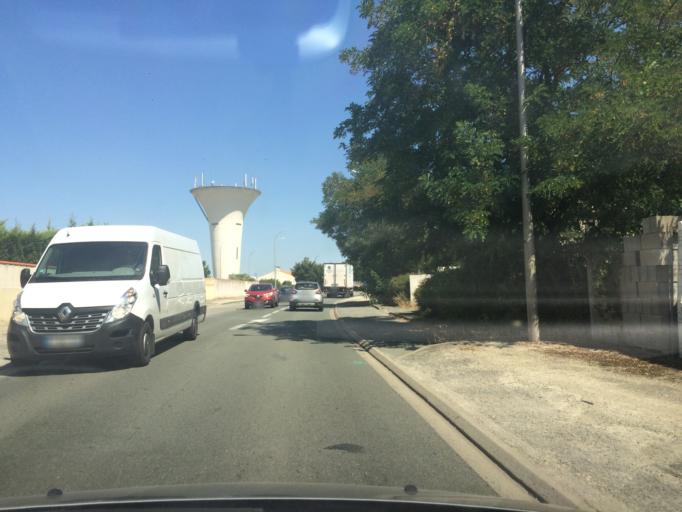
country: FR
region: Poitou-Charentes
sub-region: Departement de la Charente-Maritime
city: Charron
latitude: 46.3041
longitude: -1.0878
